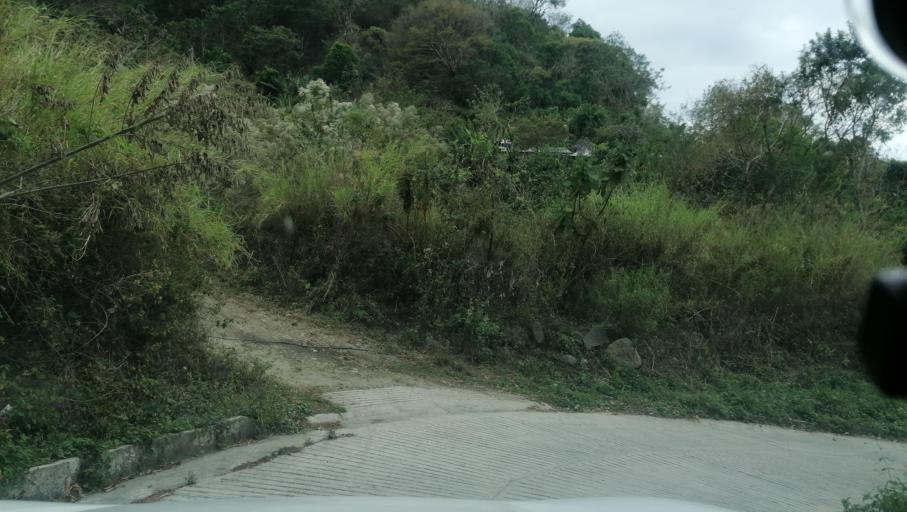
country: MX
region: Chiapas
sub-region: Cacahoatan
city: Benito Juarez
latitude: 15.1594
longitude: -92.1732
